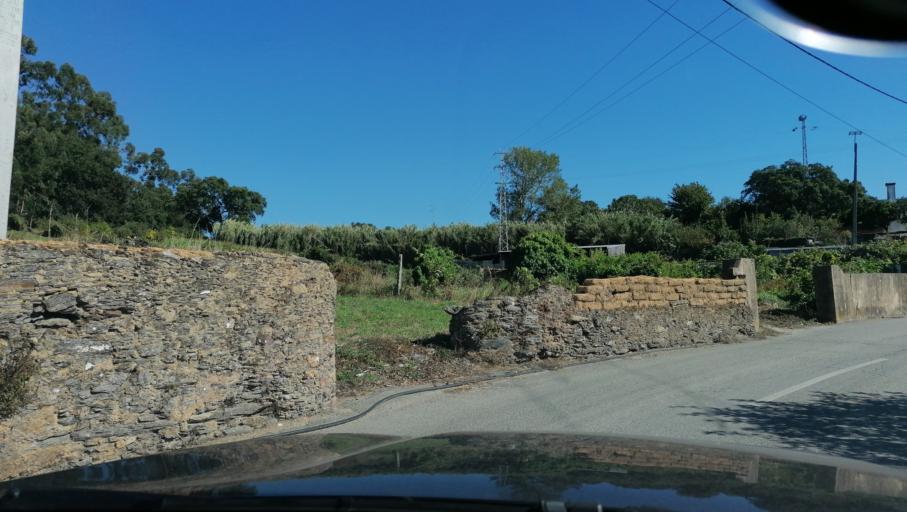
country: PT
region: Aveiro
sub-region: Estarreja
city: Beduido
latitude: 40.7532
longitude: -8.5586
